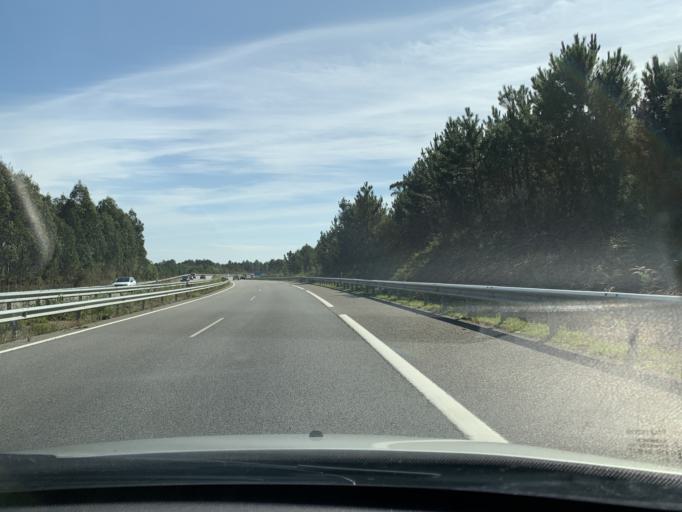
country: ES
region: Asturias
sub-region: Province of Asturias
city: Tineo
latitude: 43.5401
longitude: -6.4199
